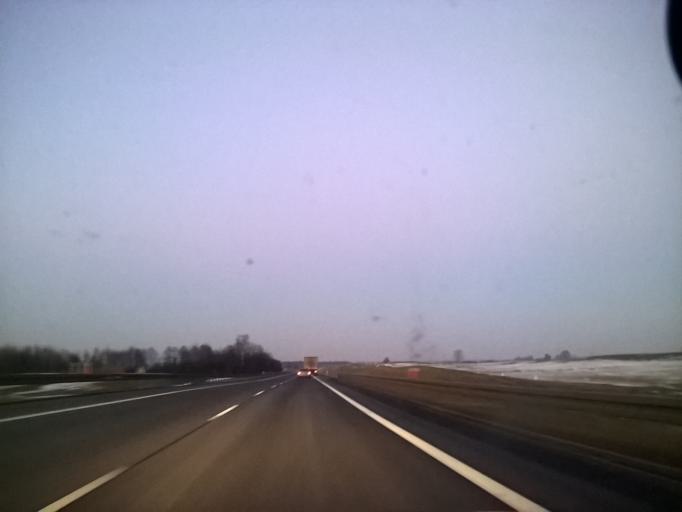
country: PL
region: Warmian-Masurian Voivodeship
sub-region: Powiat olsztynski
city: Biskupiec
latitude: 53.8406
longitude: 20.9346
